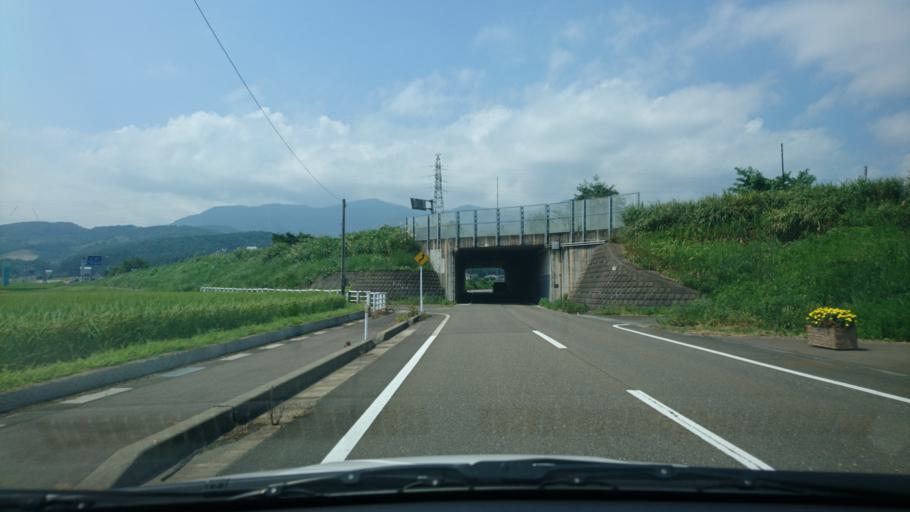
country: JP
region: Niigata
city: Arai
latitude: 37.0513
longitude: 138.2483
